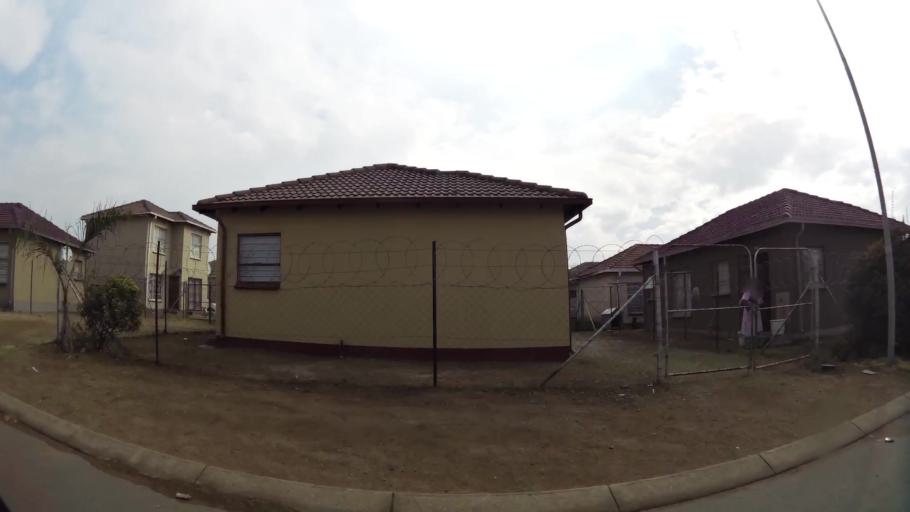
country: ZA
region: Gauteng
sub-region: Sedibeng District Municipality
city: Vanderbijlpark
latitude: -26.6846
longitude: 27.8434
